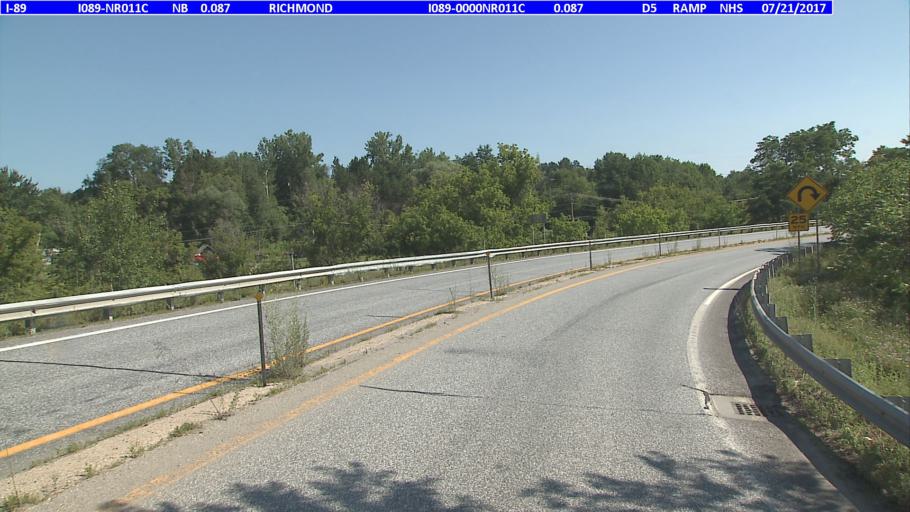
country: US
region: Vermont
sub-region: Chittenden County
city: Williston
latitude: 44.4249
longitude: -73.0110
